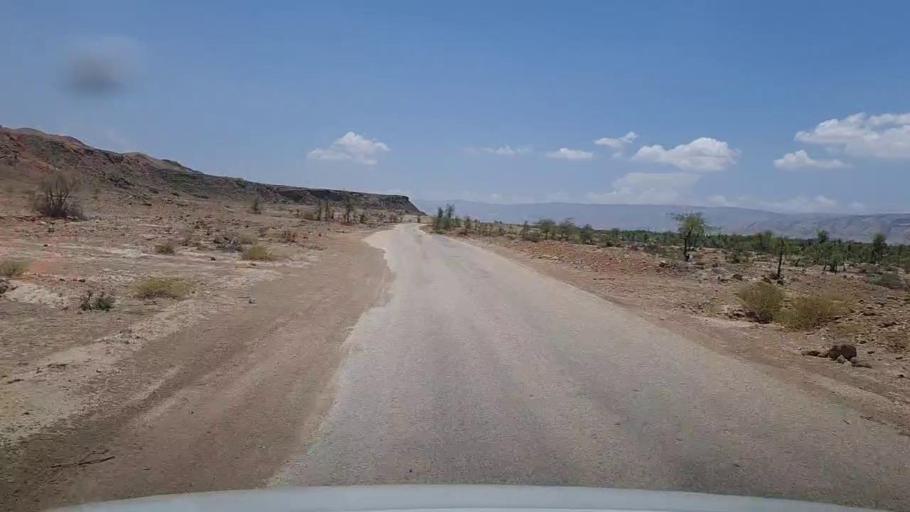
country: PK
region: Sindh
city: Bhan
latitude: 26.2977
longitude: 67.5344
